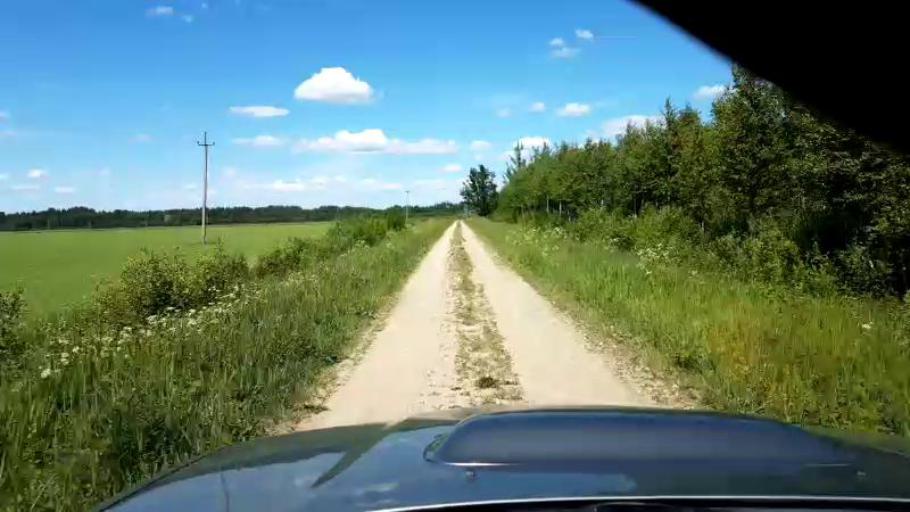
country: EE
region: Paernumaa
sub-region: Halinga vald
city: Parnu-Jaagupi
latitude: 58.5387
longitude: 24.5304
